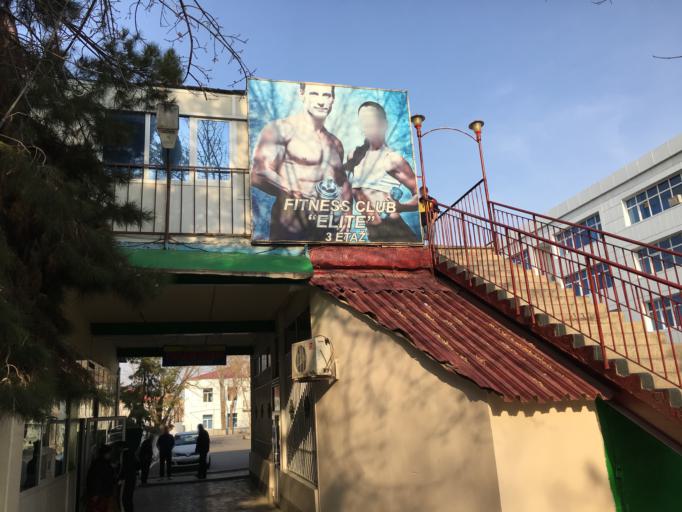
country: TM
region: Ahal
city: Ashgabat
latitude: 37.9506
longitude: 58.3679
